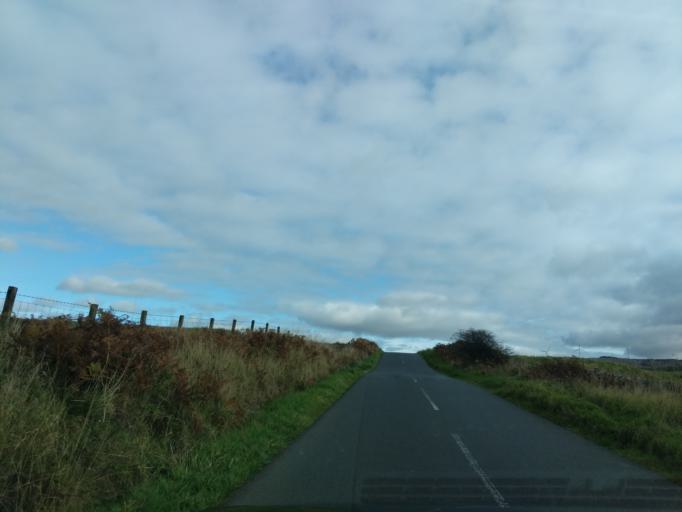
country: GB
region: Scotland
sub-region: Dumfries and Galloway
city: Castle Douglas
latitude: 55.1145
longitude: -4.0984
